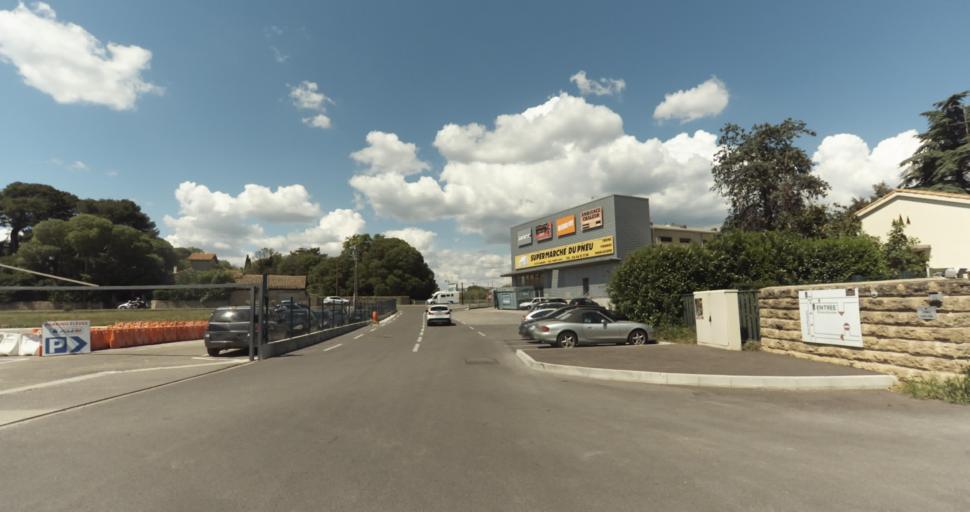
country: FR
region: Languedoc-Roussillon
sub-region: Departement du Gard
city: Milhaud
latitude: 43.8084
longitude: 4.3280
